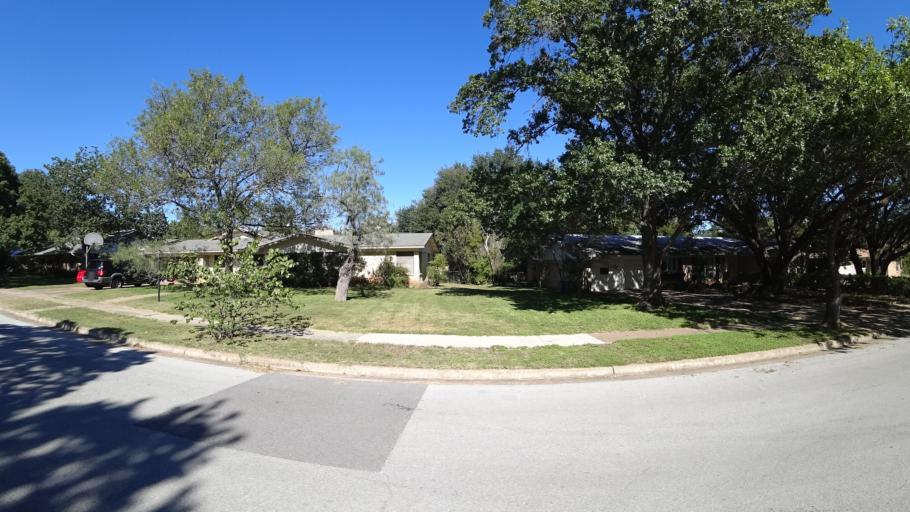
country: US
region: Texas
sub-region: Travis County
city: West Lake Hills
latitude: 30.3380
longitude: -97.7501
